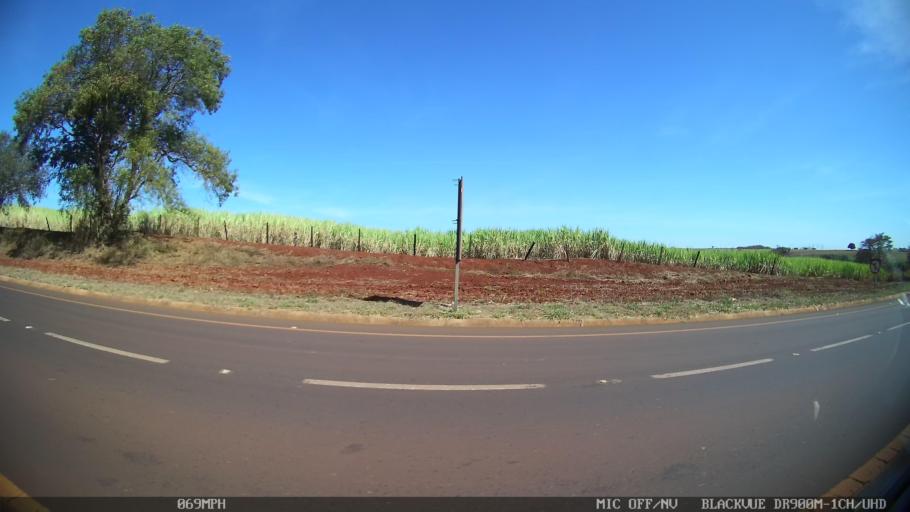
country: BR
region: Sao Paulo
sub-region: Sao Joaquim Da Barra
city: Sao Joaquim da Barra
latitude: -20.5335
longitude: -47.8290
